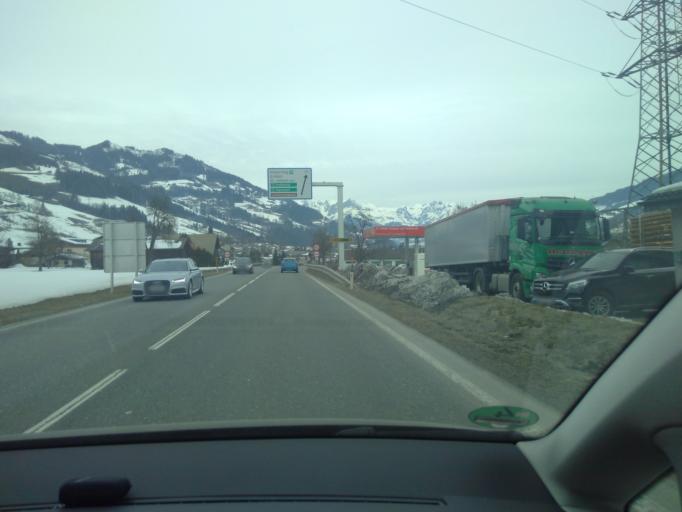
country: AT
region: Salzburg
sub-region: Politischer Bezirk Sankt Johann im Pongau
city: Sankt Johann im Pongau
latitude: 47.3364
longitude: 13.1892
